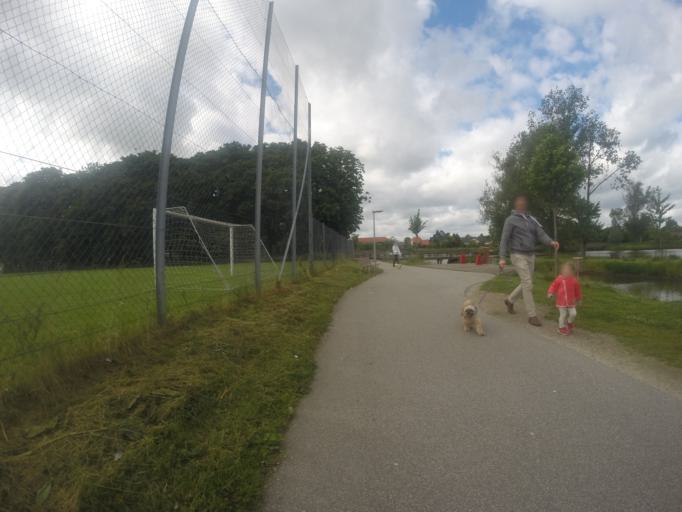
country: DK
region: Capital Region
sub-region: Hoje-Taastrup Kommune
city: Taastrup
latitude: 55.6540
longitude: 12.2974
